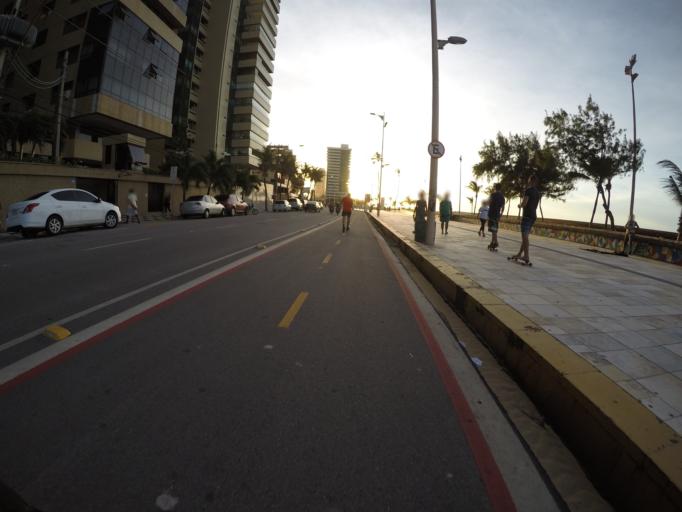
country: BR
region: Ceara
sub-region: Fortaleza
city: Fortaleza
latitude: -3.7207
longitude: -38.5102
